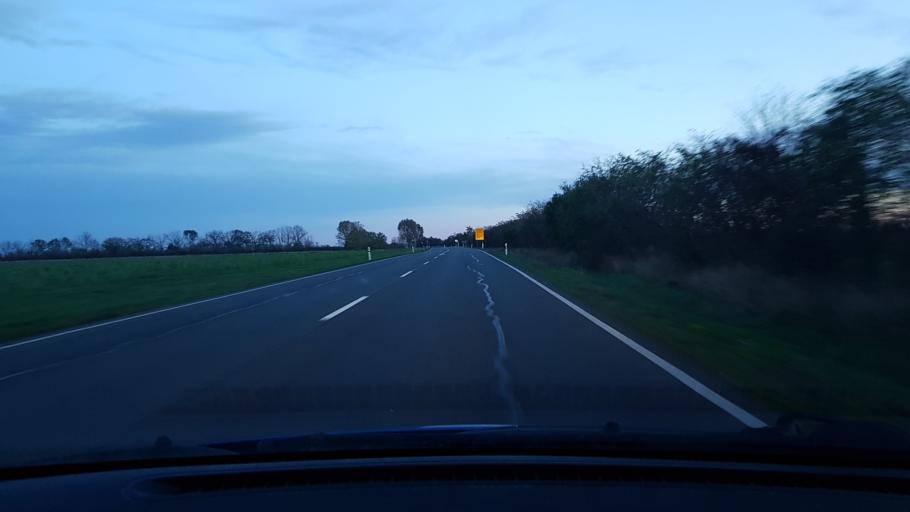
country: DE
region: Saxony-Anhalt
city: Zerbst
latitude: 51.9948
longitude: 12.0389
